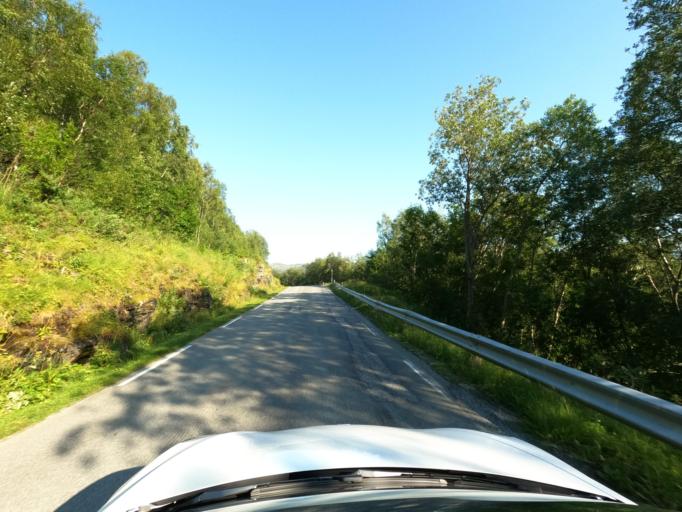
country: NO
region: Nordland
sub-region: Narvik
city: Bjerkvik
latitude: 68.5531
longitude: 17.5760
